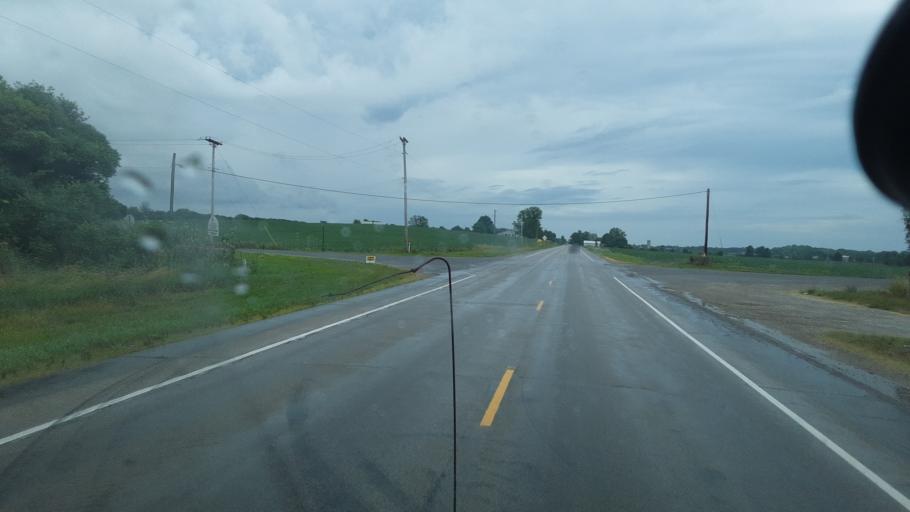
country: US
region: Indiana
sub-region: Steuben County
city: Hamilton
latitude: 41.6302
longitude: -84.8377
